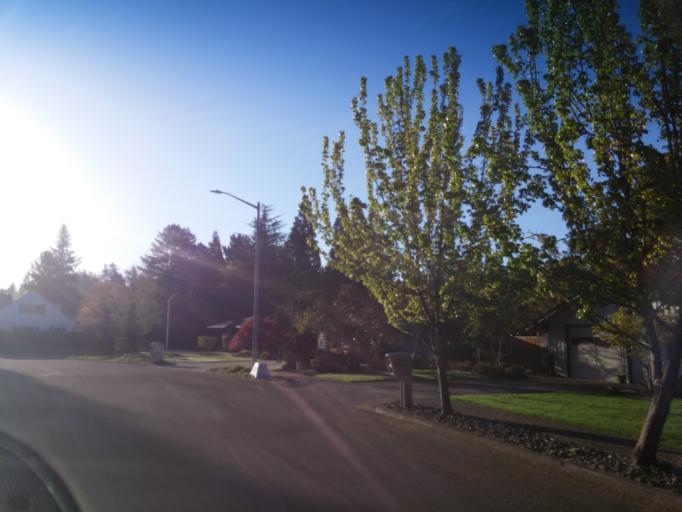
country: US
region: Oregon
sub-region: Washington County
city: Cedar Hills
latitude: 45.5030
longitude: -122.7914
